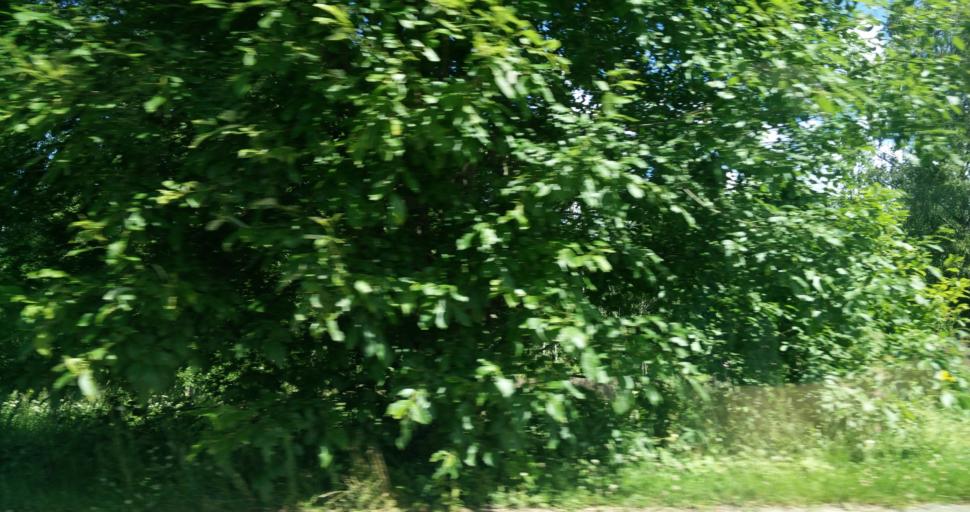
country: SE
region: Vaermland
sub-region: Hagfors Kommun
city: Hagfors
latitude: 60.0249
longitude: 13.6797
